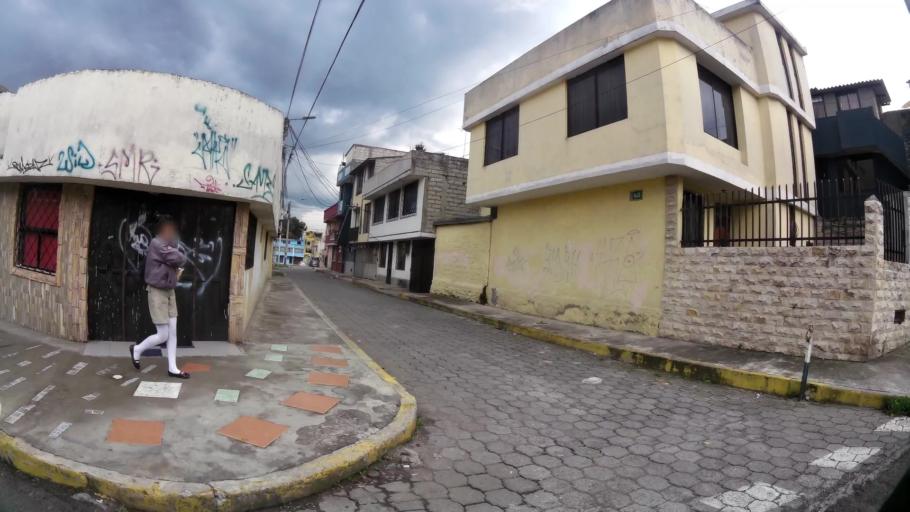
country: EC
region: Pichincha
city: Quito
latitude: -0.2834
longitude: -78.5424
